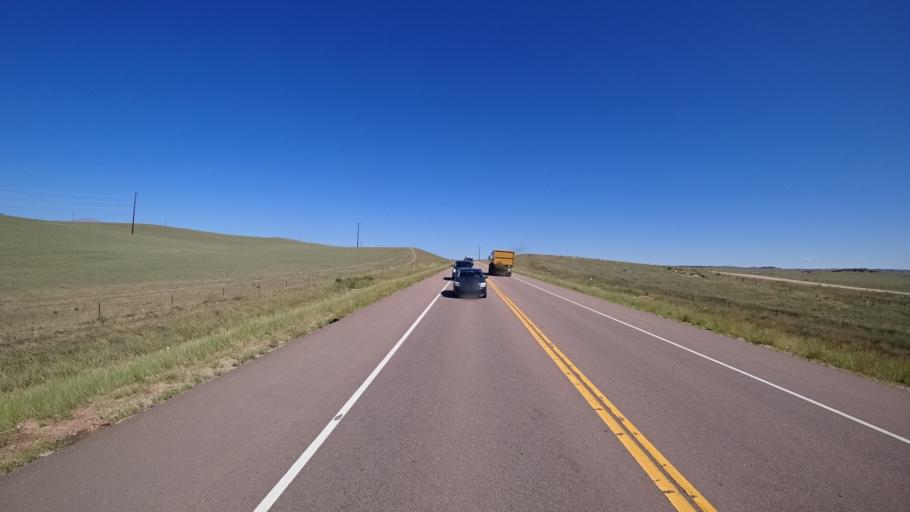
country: US
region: Colorado
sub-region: El Paso County
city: Cimarron Hills
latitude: 38.7986
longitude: -104.6602
